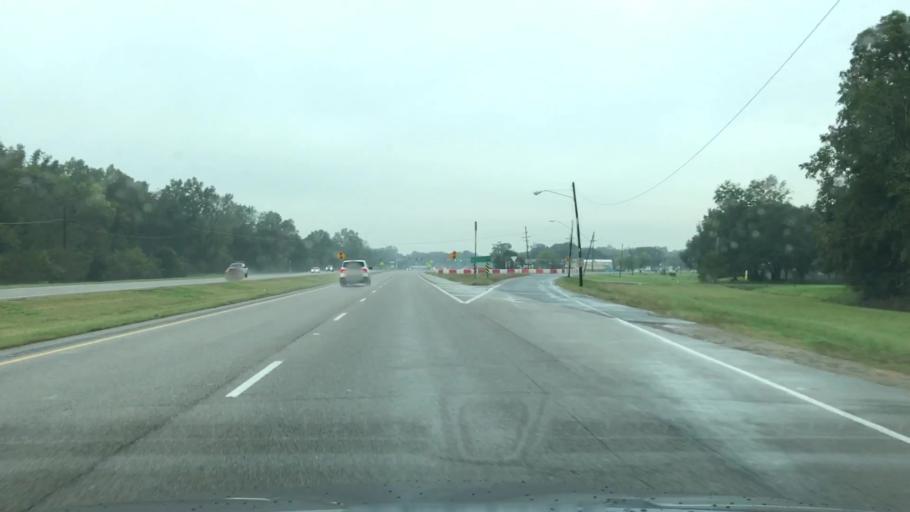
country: US
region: Louisiana
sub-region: Saint Charles Parish
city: Des Allemands
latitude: 29.8272
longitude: -90.4615
